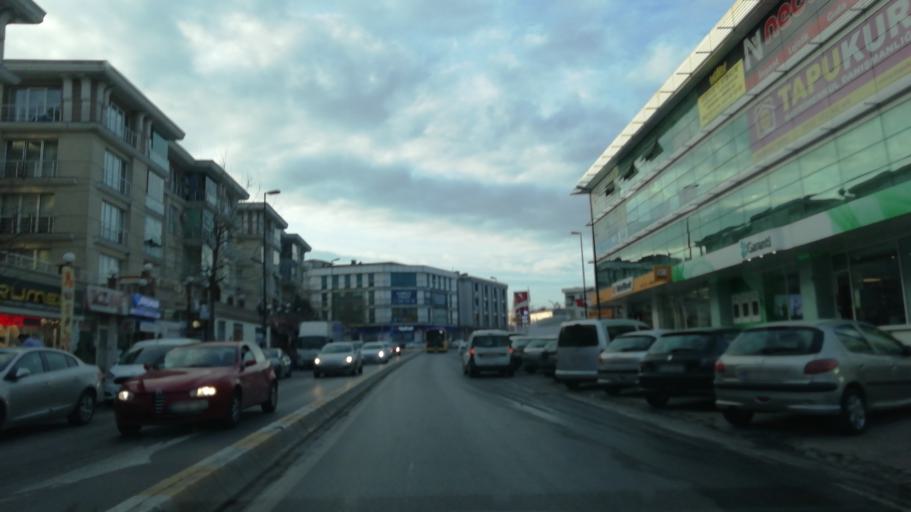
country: TR
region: Istanbul
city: Mahmutbey
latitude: 41.0162
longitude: 28.8247
